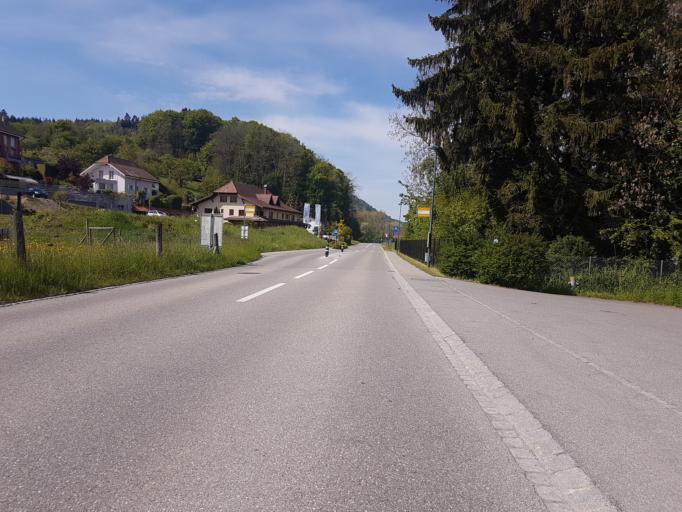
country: CH
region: Bern
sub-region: Seeland District
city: Erlach
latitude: 47.0456
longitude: 7.1476
